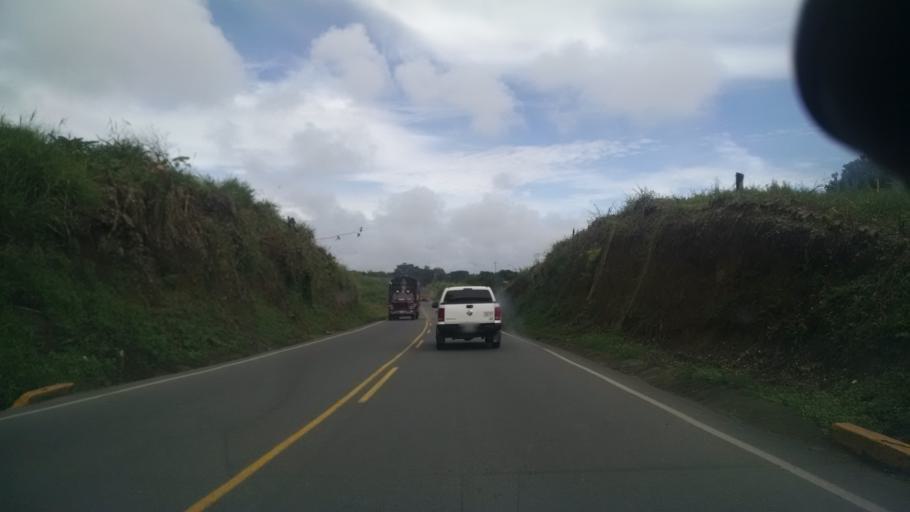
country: CO
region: Caldas
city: Palestina
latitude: 5.0784
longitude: -75.6481
